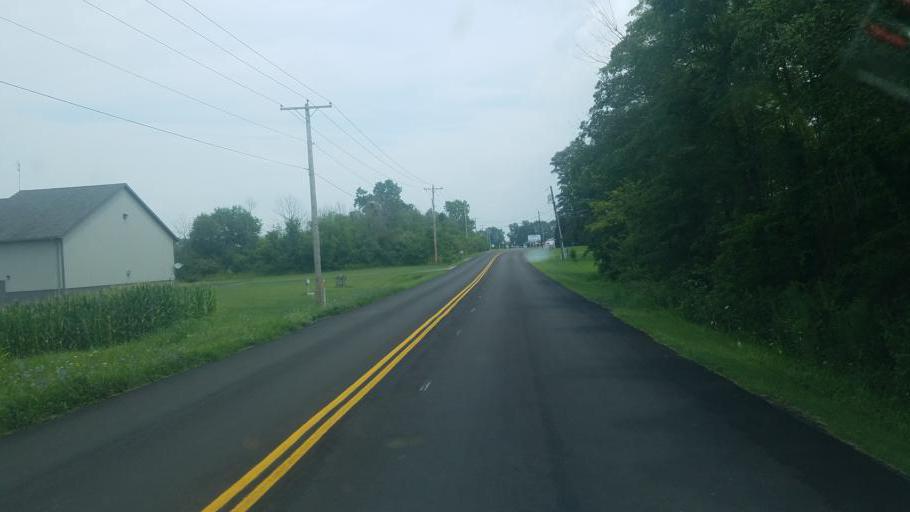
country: US
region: Ohio
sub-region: Logan County
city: Russells Point
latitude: 40.4711
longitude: -83.8460
